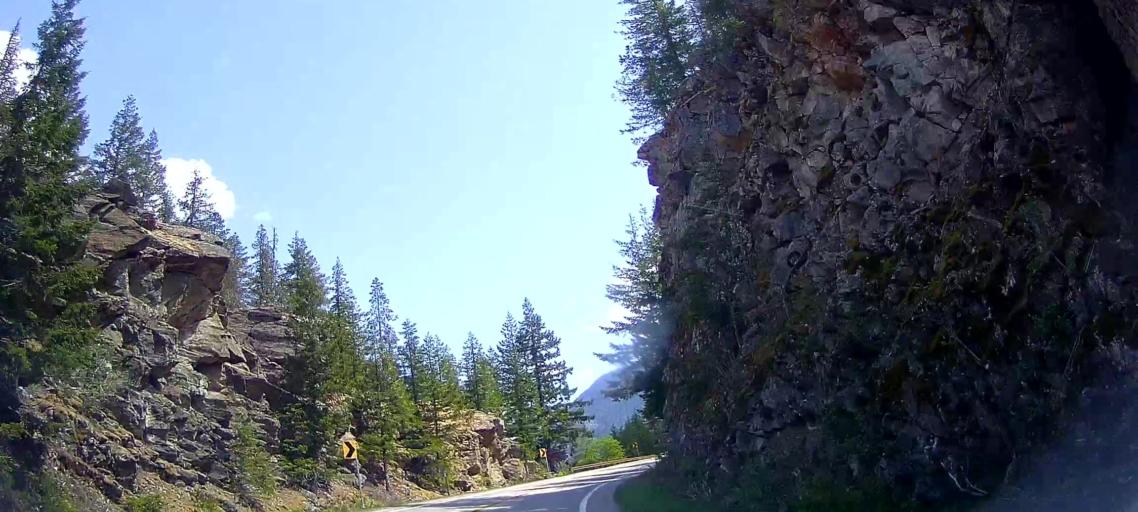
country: US
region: Washington
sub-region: Snohomish County
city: Darrington
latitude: 48.7116
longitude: -121.1321
